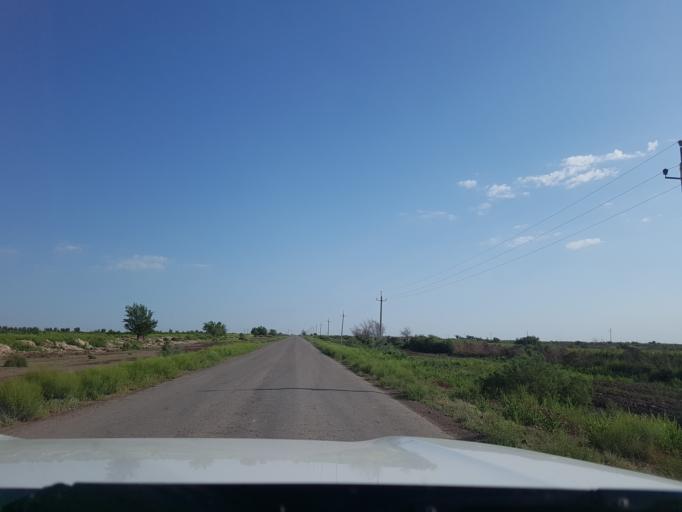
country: TM
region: Dasoguz
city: Koeneuergench
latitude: 41.8565
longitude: 58.7053
